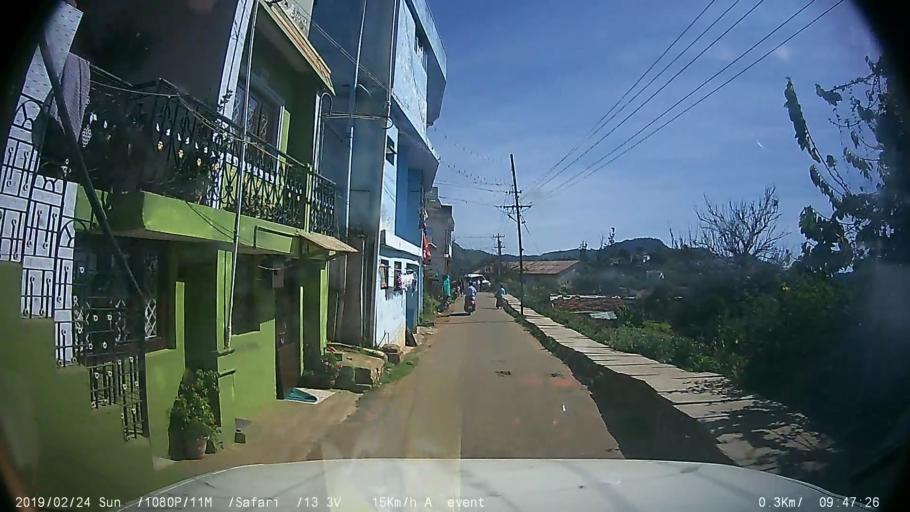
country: IN
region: Tamil Nadu
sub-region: Nilgiri
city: Wellington
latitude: 11.3481
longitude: 76.7796
